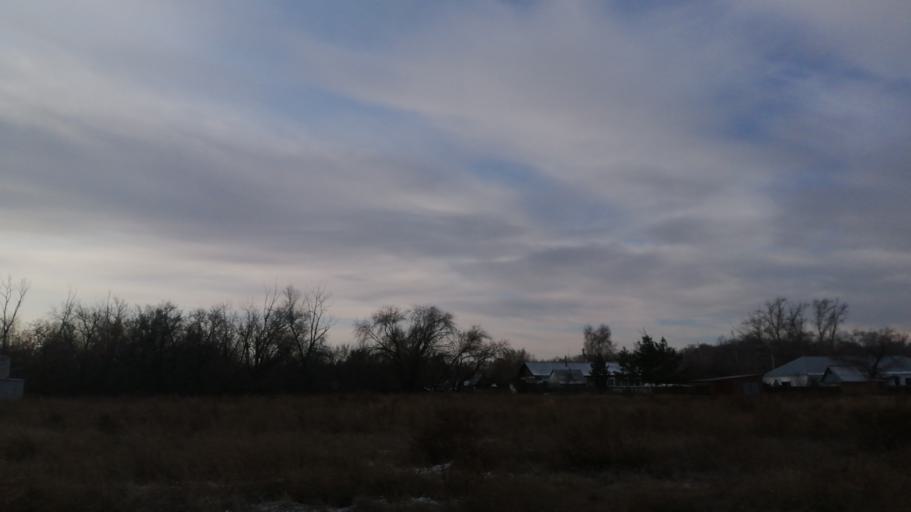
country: RU
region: Novosibirsk
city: Krasnozerskoye
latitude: 53.9887
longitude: 78.7250
